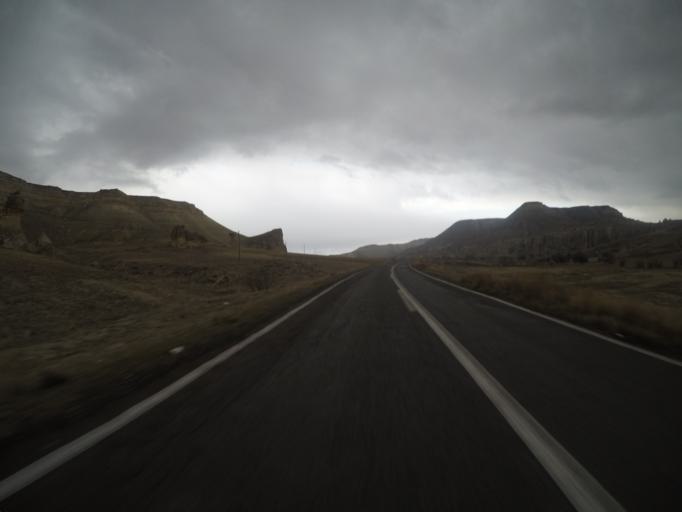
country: TR
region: Nevsehir
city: Avanos
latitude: 38.6805
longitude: 34.8441
